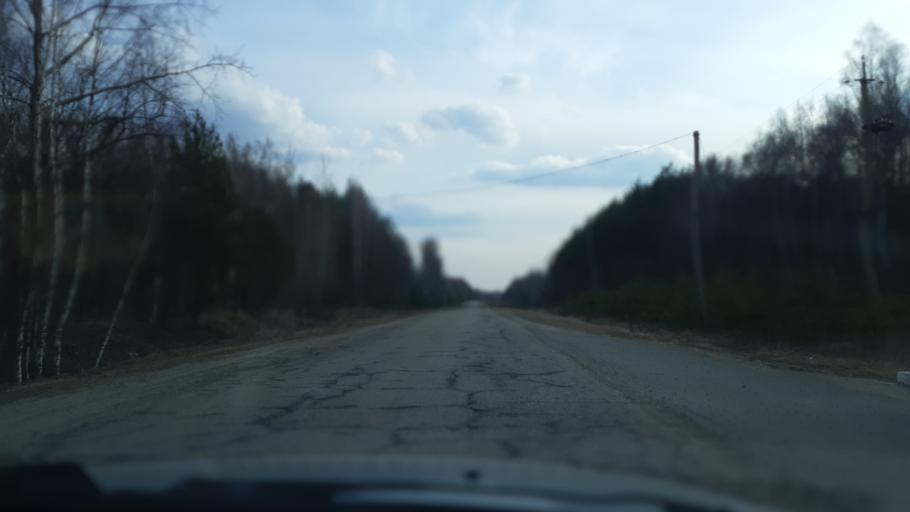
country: RU
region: Vladimir
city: Nikologory
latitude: 56.1186
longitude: 41.9860
